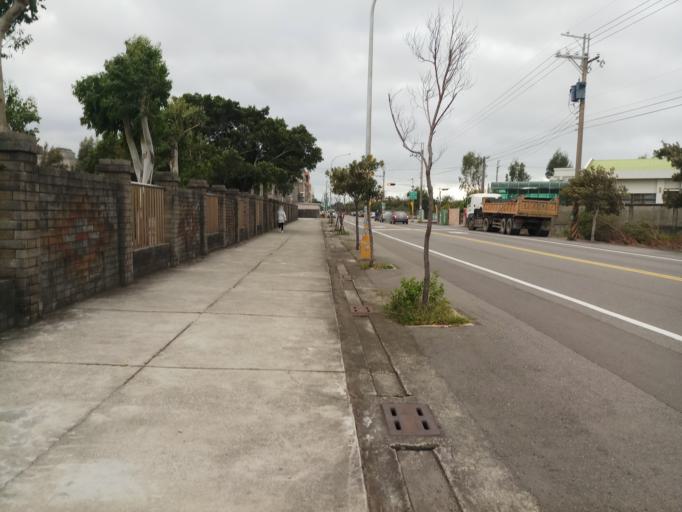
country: TW
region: Taiwan
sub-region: Miaoli
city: Miaoli
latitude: 24.6791
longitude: 120.8632
